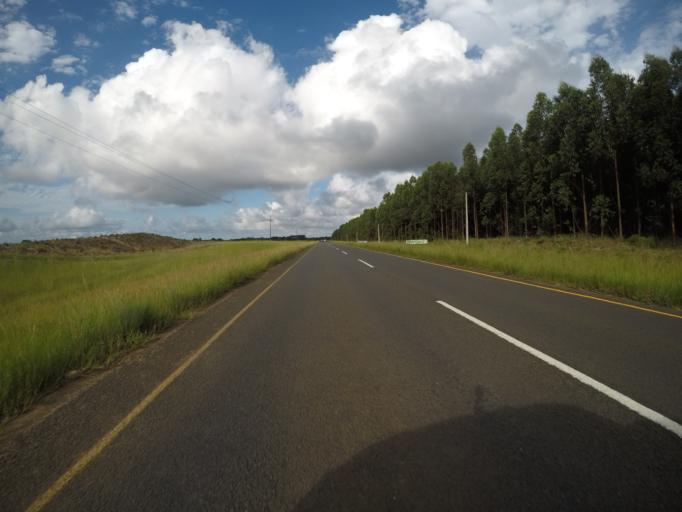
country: ZA
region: KwaZulu-Natal
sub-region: uMkhanyakude District Municipality
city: Mtubatuba
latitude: -28.3840
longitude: 32.2397
